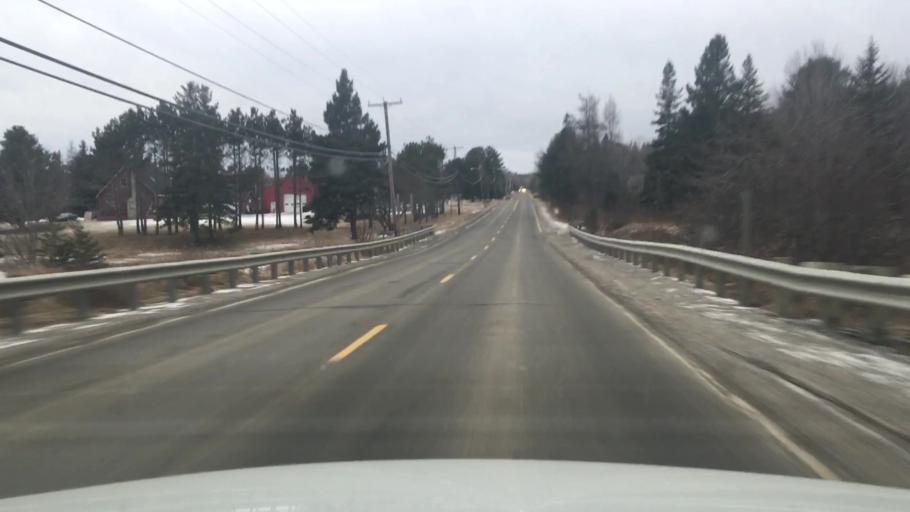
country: US
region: Maine
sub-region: Hancock County
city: Trenton
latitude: 44.5006
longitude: -68.3495
